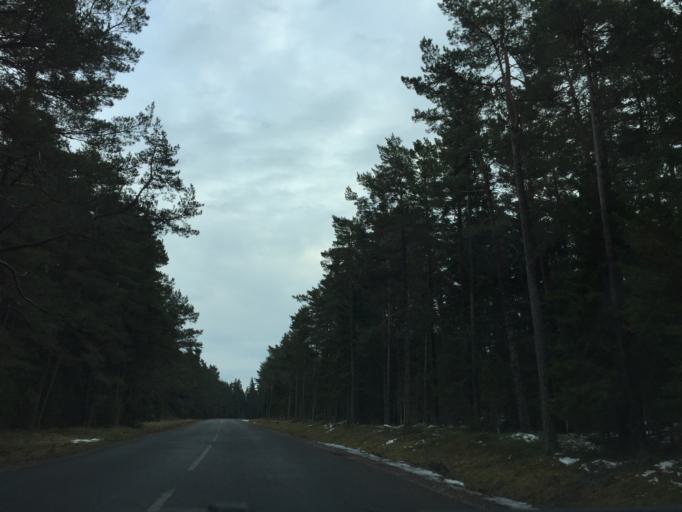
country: EE
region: Saare
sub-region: Kuressaare linn
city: Kuressaare
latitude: 58.4355
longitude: 22.0645
